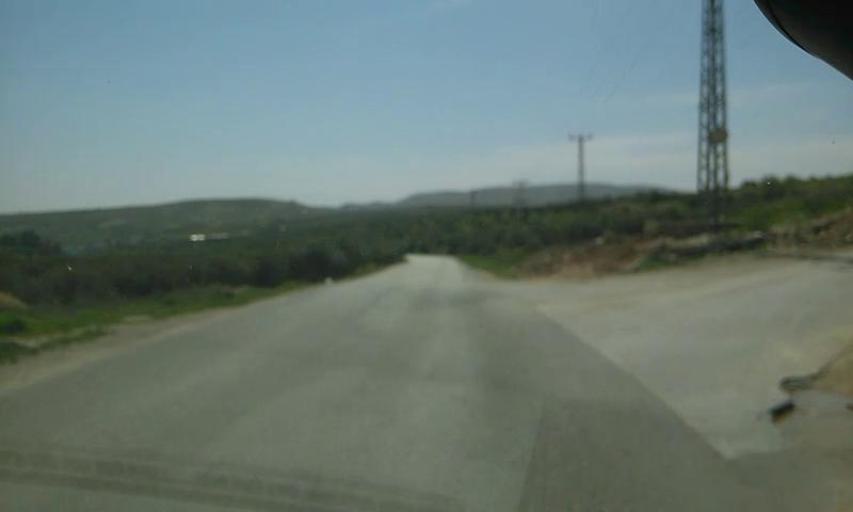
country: PS
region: West Bank
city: Marah Rabbah
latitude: 31.6333
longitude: 35.2028
